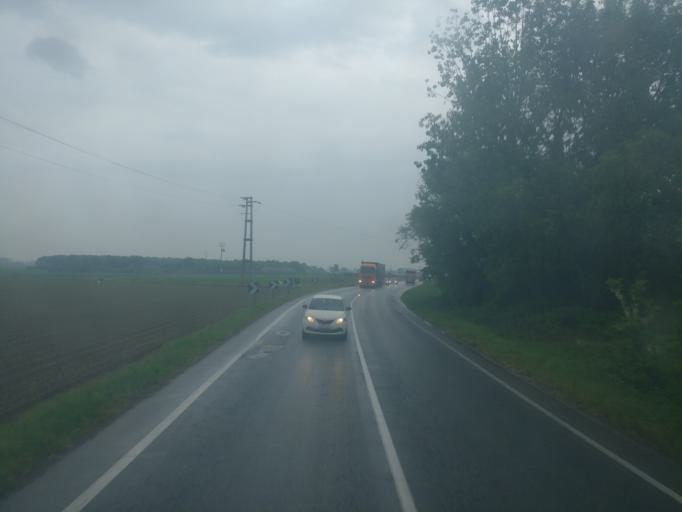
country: IT
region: Piedmont
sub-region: Provincia di Torino
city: Carignano
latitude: 44.9205
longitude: 7.6739
